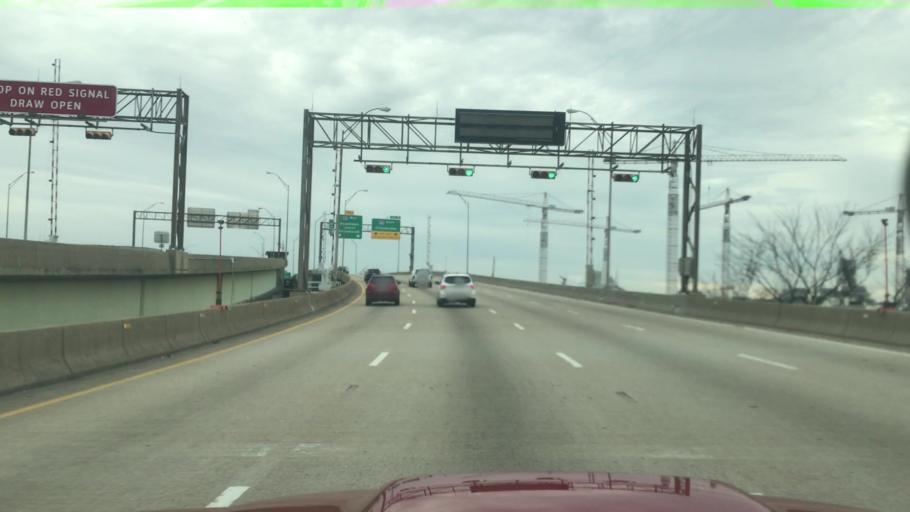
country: US
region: Virginia
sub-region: City of Norfolk
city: Norfolk
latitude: 36.8434
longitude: -76.2856
